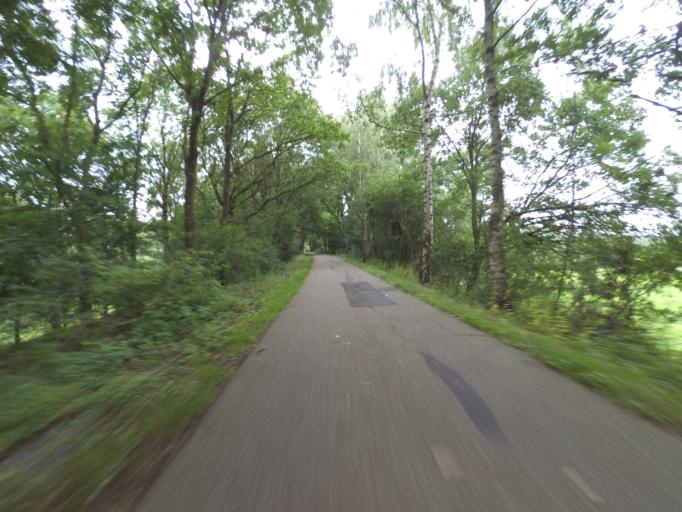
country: DE
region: North Rhine-Westphalia
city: Stolberg
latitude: 50.7659
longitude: 6.1666
